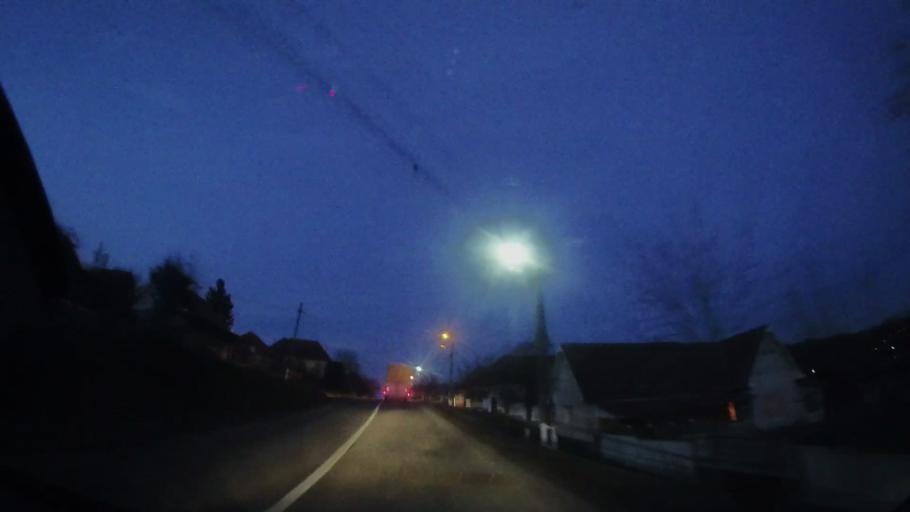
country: RO
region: Mures
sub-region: Comuna Sarmasu
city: Sarmasu
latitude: 46.7818
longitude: 24.2028
